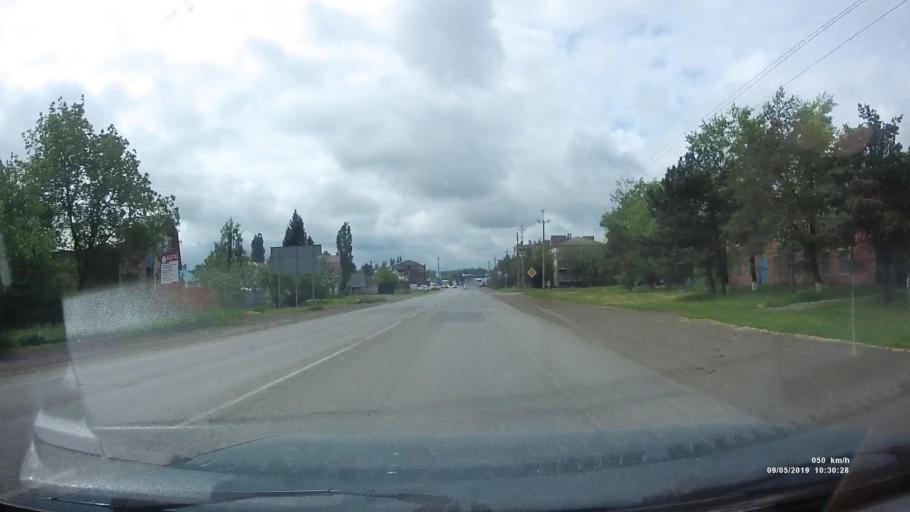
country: RU
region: Rostov
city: Azov
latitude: 47.0897
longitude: 39.4301
